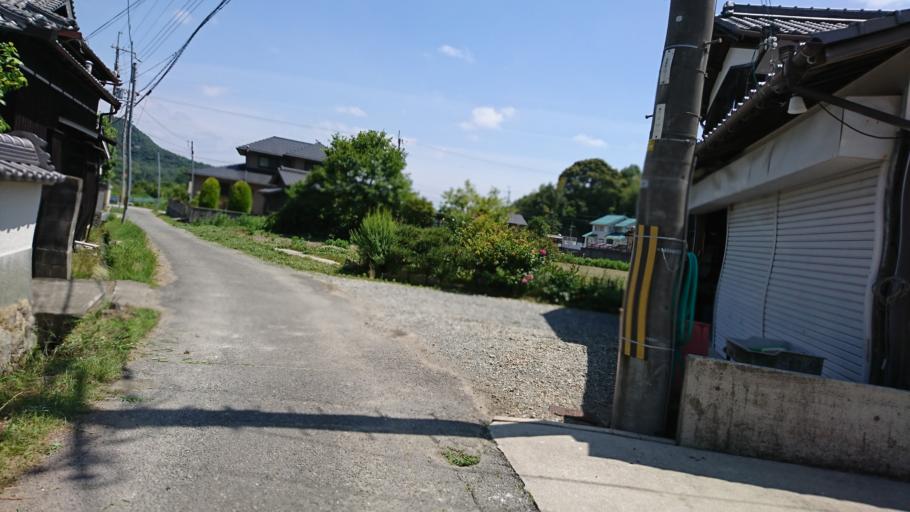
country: JP
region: Hyogo
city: Kakogawacho-honmachi
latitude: 34.8089
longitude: 134.7852
